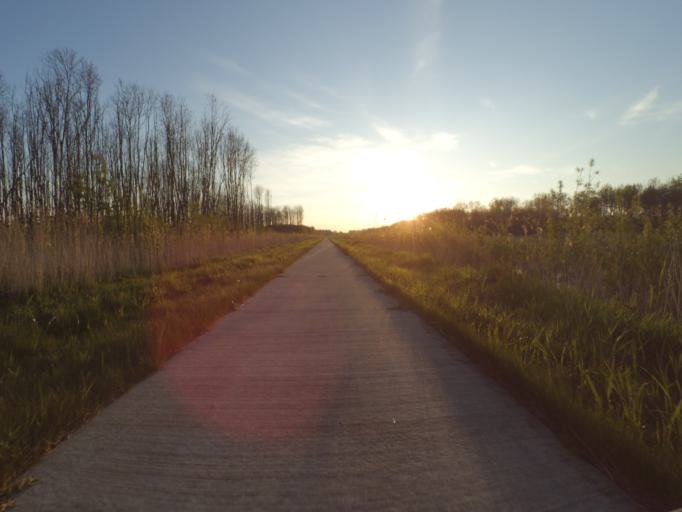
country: NL
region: Flevoland
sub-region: Gemeente Zeewolde
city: Zeewolde
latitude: 52.3405
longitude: 5.4515
